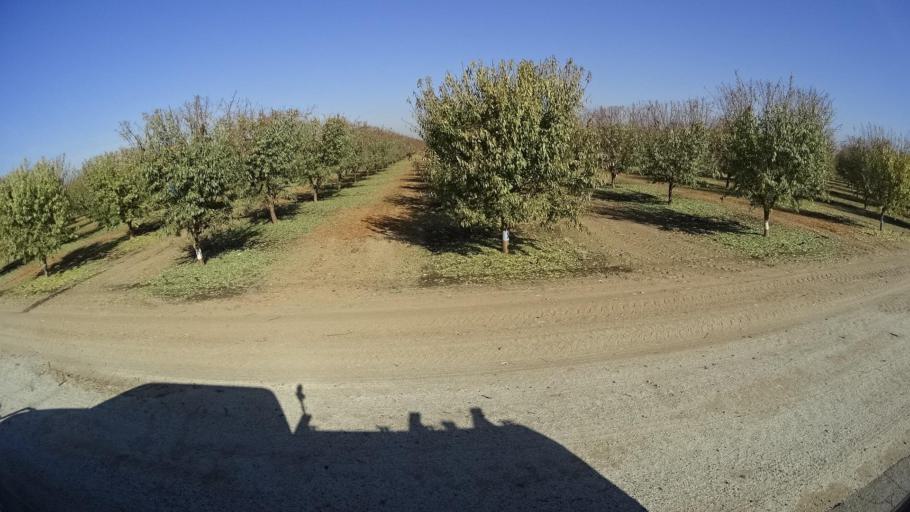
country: US
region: California
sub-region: Kern County
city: McFarland
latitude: 35.7180
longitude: -119.2163
